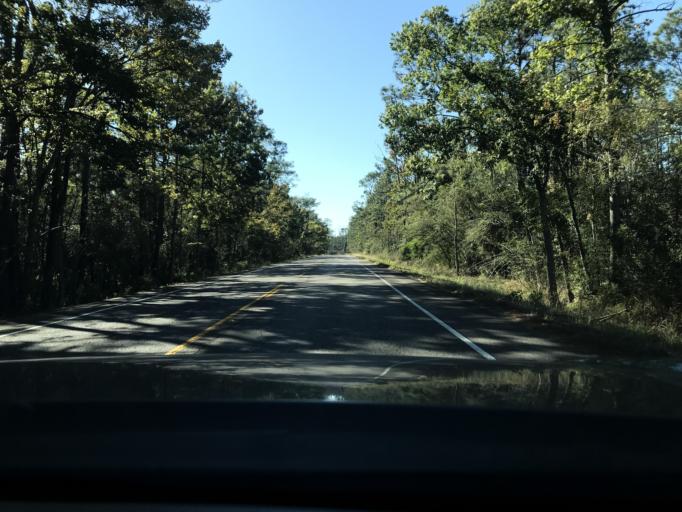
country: US
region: Louisiana
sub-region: Calcasieu Parish
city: Moss Bluff
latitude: 30.3052
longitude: -93.2537
